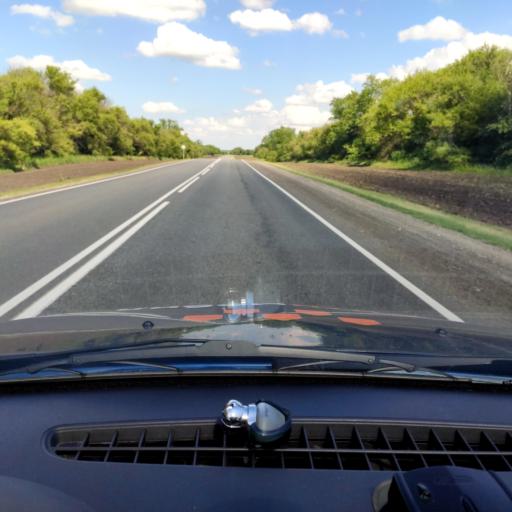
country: RU
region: Orjol
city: Livny
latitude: 52.4293
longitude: 37.7882
